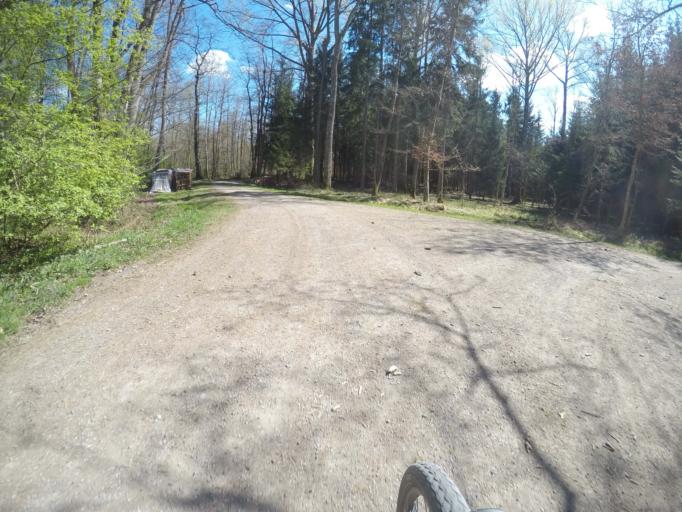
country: DE
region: Baden-Wuerttemberg
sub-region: Regierungsbezirk Stuttgart
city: Altdorf
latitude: 48.6063
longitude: 9.0178
